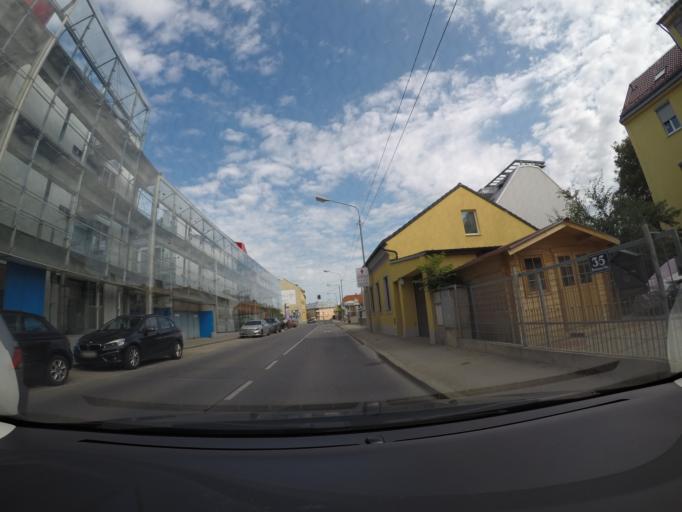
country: AT
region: Lower Austria
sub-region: Politischer Bezirk Modling
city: Brunn am Gebirge
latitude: 48.1431
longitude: 16.2979
